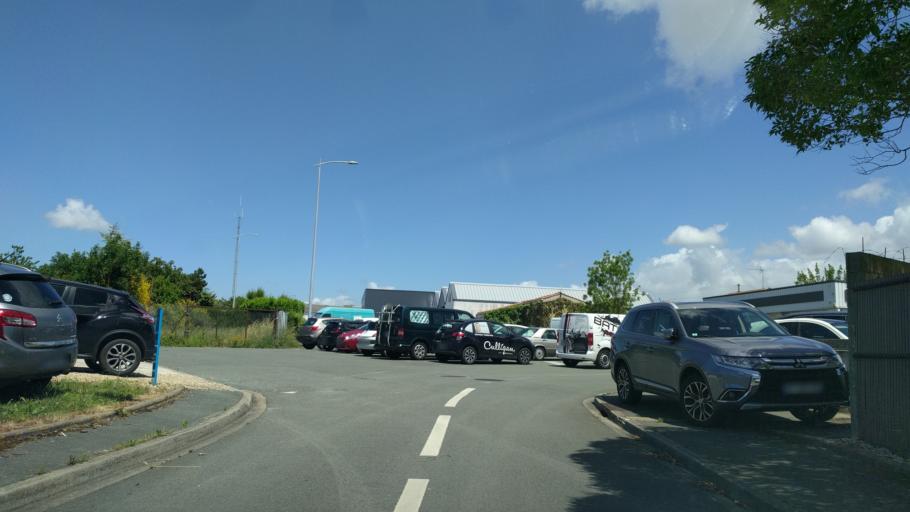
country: FR
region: Poitou-Charentes
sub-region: Departement de la Charente-Maritime
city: Perigny
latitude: 46.1576
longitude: -1.1207
